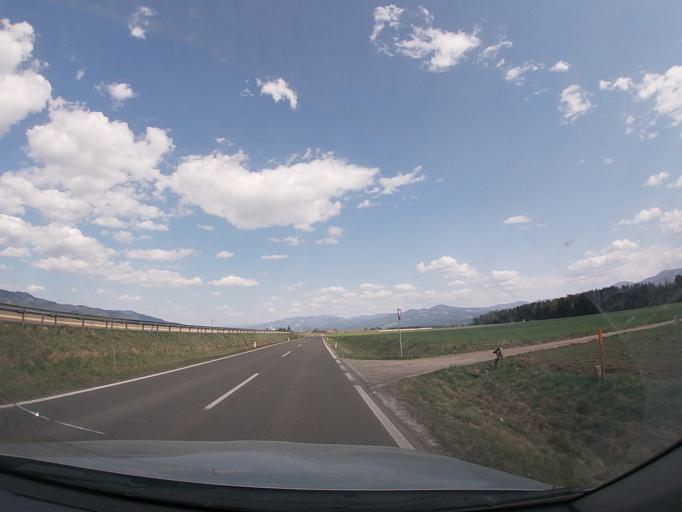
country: AT
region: Styria
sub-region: Politischer Bezirk Murtal
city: Fohnsdorf
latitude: 47.1861
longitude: 14.6928
